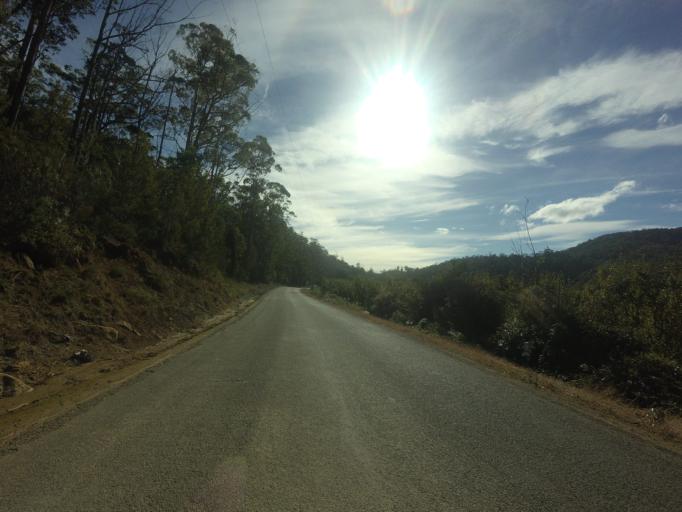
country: AU
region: Tasmania
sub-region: Clarence
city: Sandford
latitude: -43.1234
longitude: 147.7615
